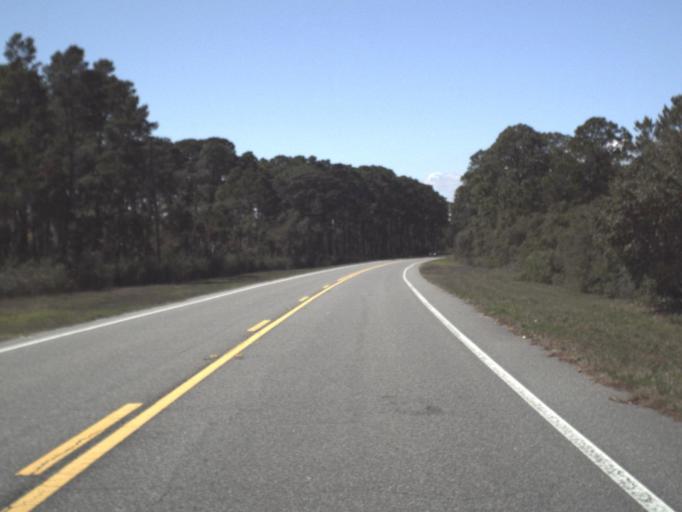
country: US
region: Florida
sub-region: Franklin County
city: Carrabelle
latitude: 29.9272
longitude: -84.4298
